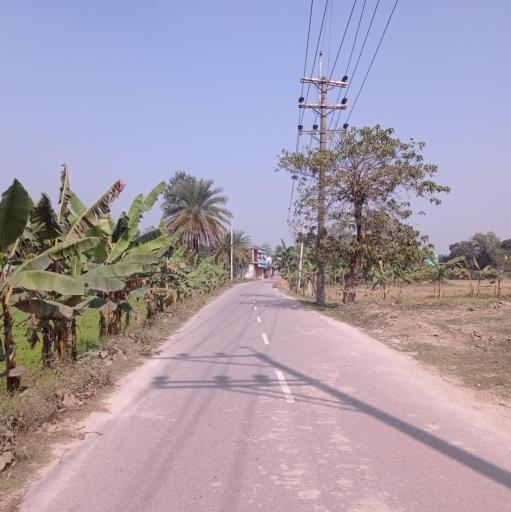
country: BD
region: Dhaka
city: Narsingdi
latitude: 24.0819
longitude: 90.6945
